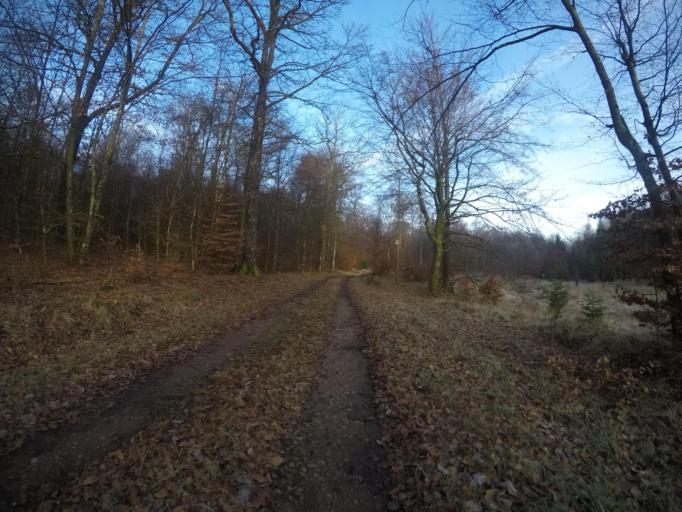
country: BE
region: Wallonia
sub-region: Province du Luxembourg
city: Habay-la-Vieille
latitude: 49.7652
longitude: 5.6584
